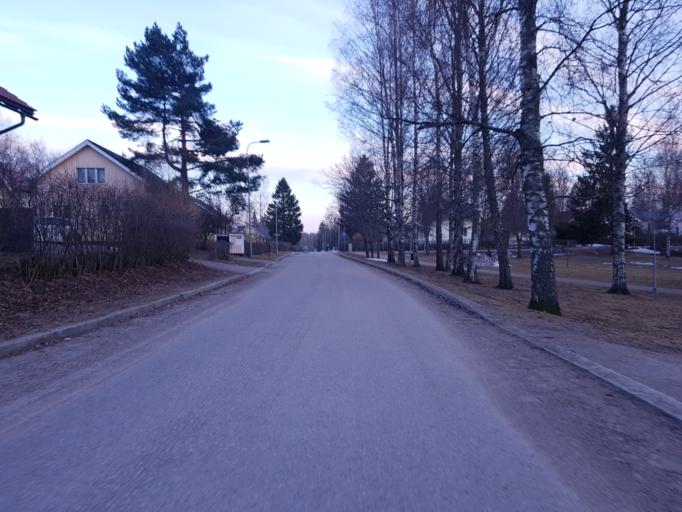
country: FI
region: Uusimaa
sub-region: Helsinki
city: Vantaa
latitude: 60.2623
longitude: 24.9538
